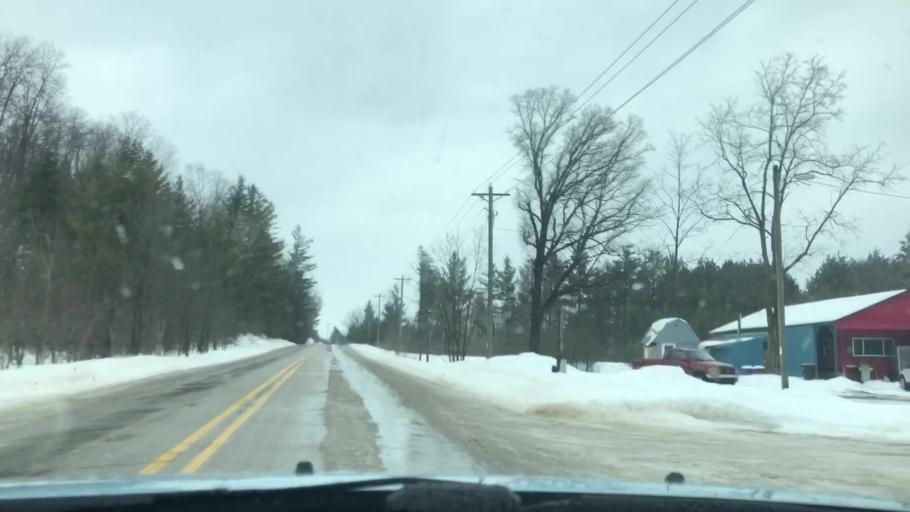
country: US
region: Michigan
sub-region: Charlevoix County
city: East Jordan
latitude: 45.1074
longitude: -85.1286
